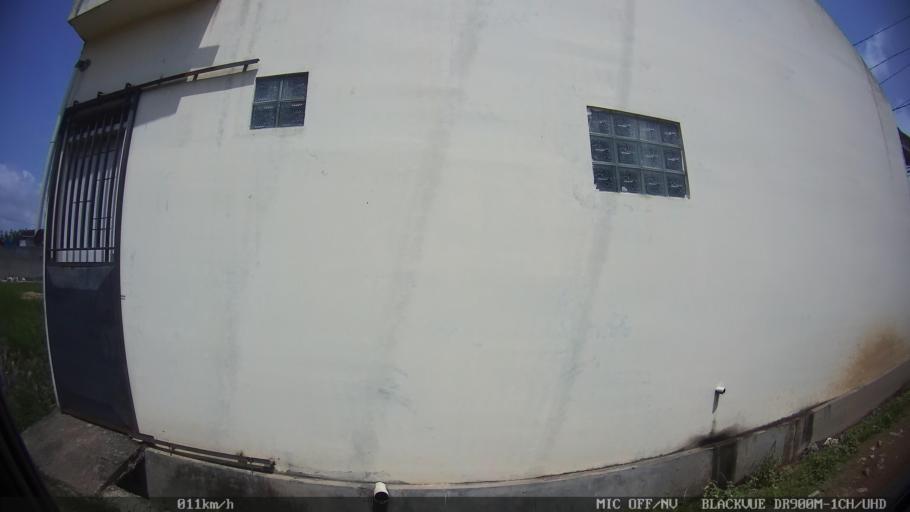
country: ID
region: Lampung
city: Kedaton
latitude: -5.3513
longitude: 105.2834
